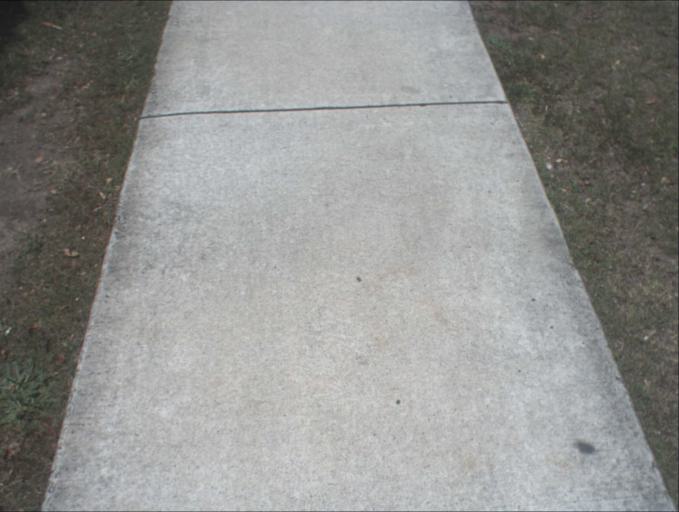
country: AU
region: Queensland
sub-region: Logan
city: Logan City
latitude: -27.6741
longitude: 153.0952
